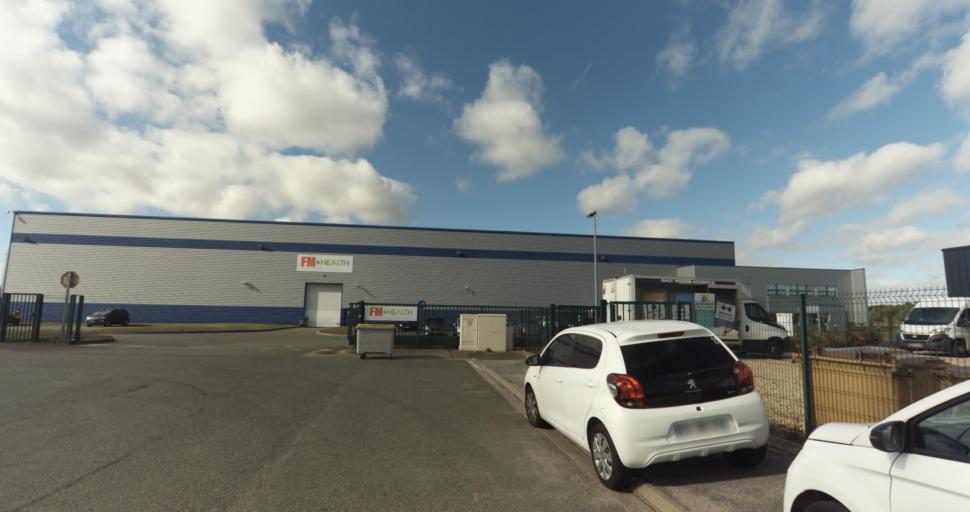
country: FR
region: Centre
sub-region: Departement d'Eure-et-Loir
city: Garnay
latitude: 48.7279
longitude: 1.3202
